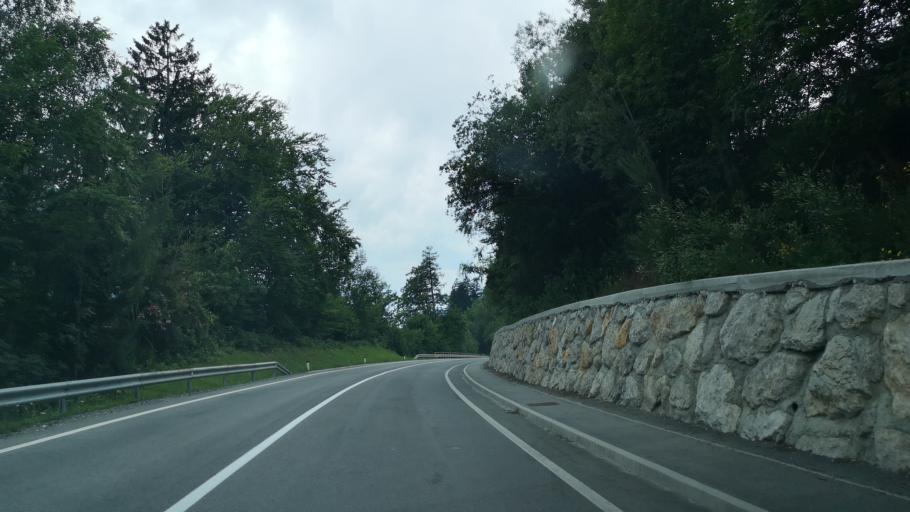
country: SI
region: Jesenice
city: Hrusica
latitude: 46.4438
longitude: 14.0327
